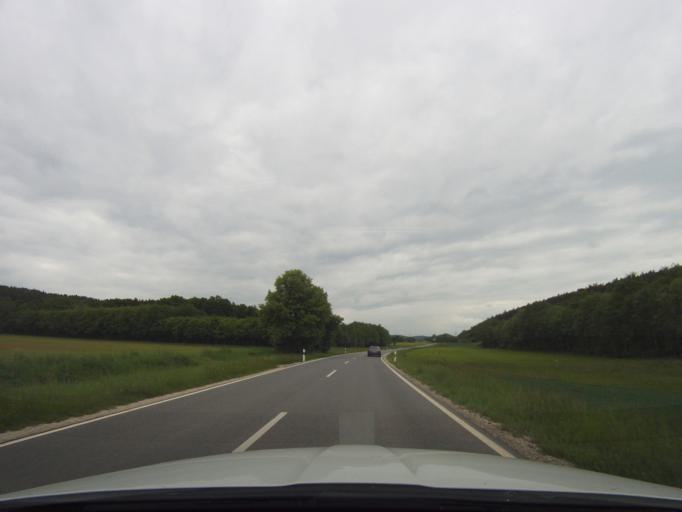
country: DE
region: Bavaria
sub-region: Upper Franconia
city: Altendorf
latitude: 50.1113
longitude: 11.1864
